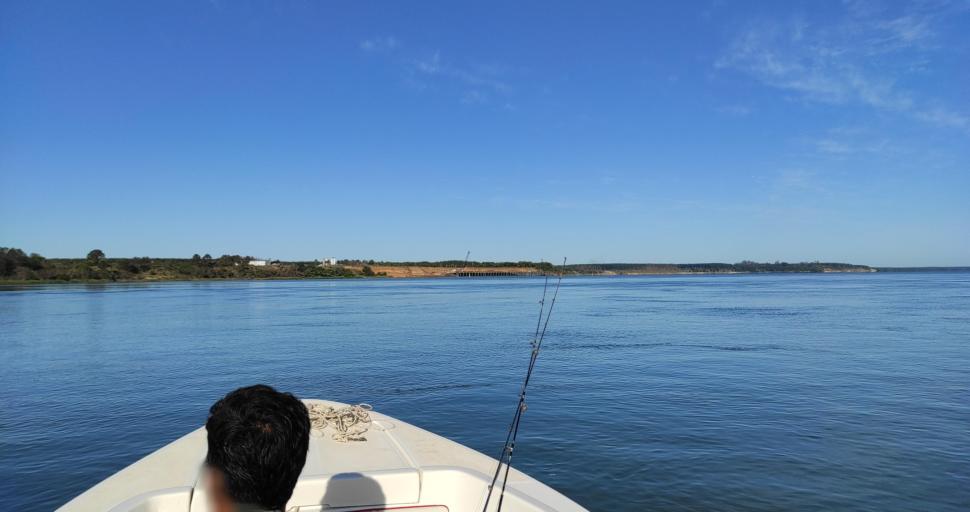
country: AR
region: Corrientes
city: Ituzaingo
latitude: -27.6051
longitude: -56.8261
